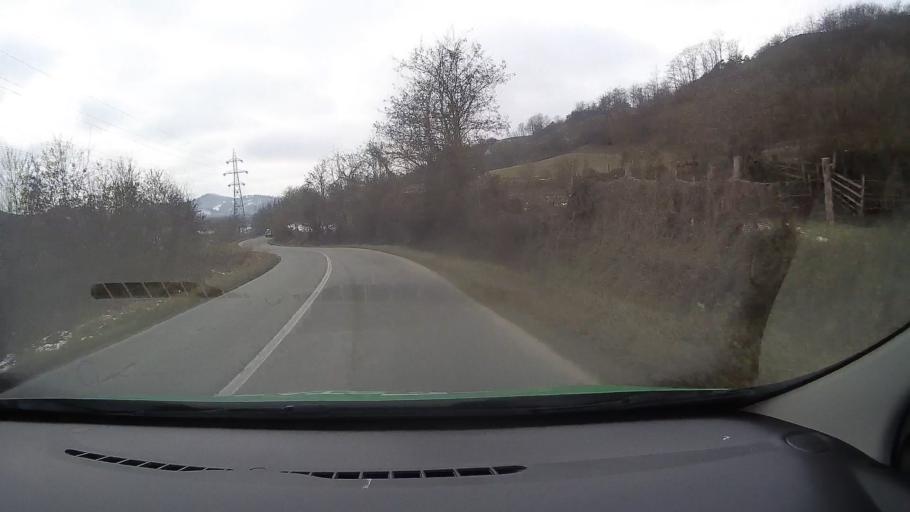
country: RO
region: Alba
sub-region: Oras Zlatna
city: Fenes
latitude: 46.0942
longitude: 23.2934
